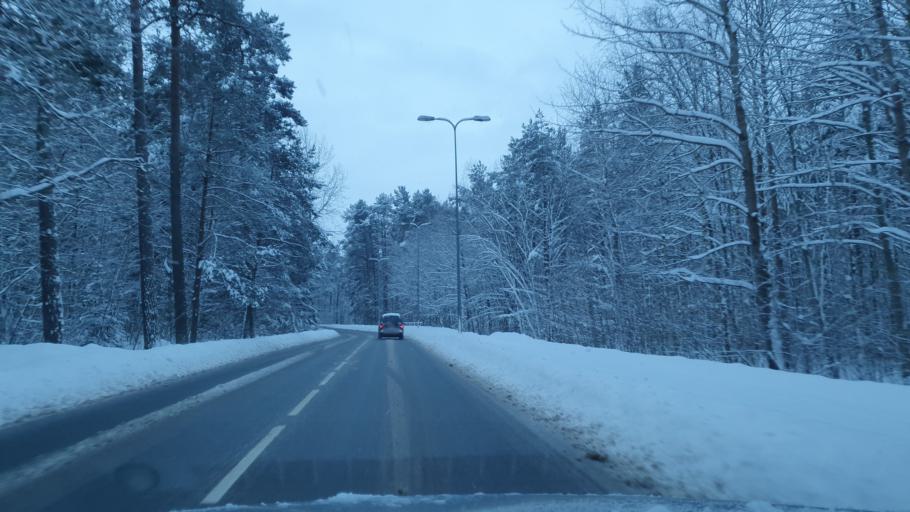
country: EE
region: Harju
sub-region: Viimsi vald
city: Viimsi
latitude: 59.4774
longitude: 24.8467
